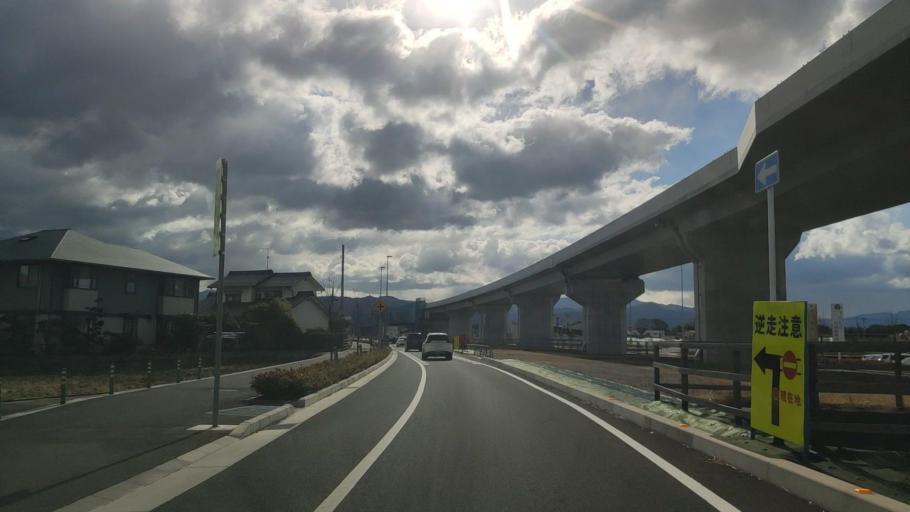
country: JP
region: Ehime
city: Masaki-cho
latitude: 33.8151
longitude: 132.7205
